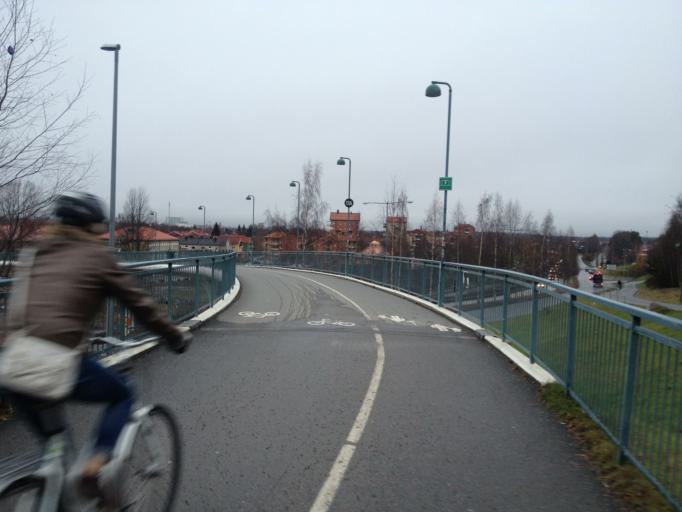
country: SE
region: Vaesterbotten
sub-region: Umea Kommun
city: Umea
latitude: 63.8195
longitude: 20.2948
